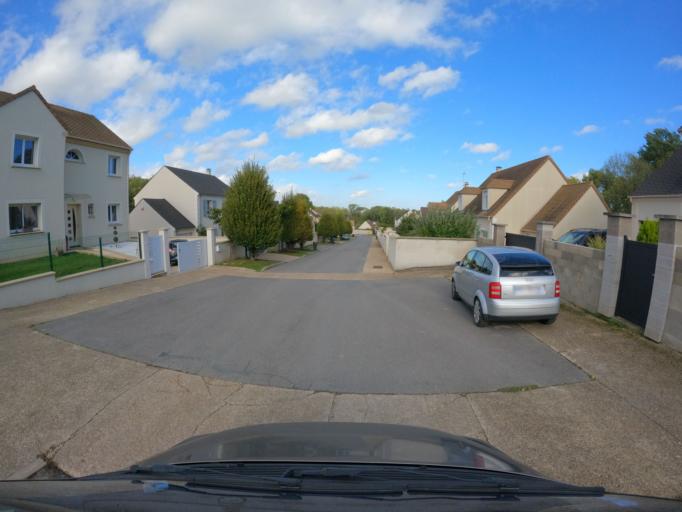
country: FR
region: Ile-de-France
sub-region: Departement de Seine-et-Marne
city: Montry
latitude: 48.8906
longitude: 2.8161
